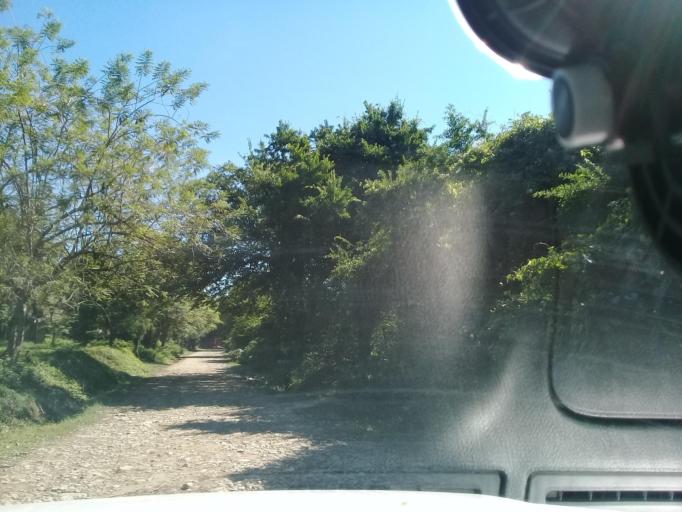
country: MX
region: Hidalgo
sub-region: Huejutla de Reyes
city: Huejutla de Reyes
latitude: 21.1605
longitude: -98.4090
